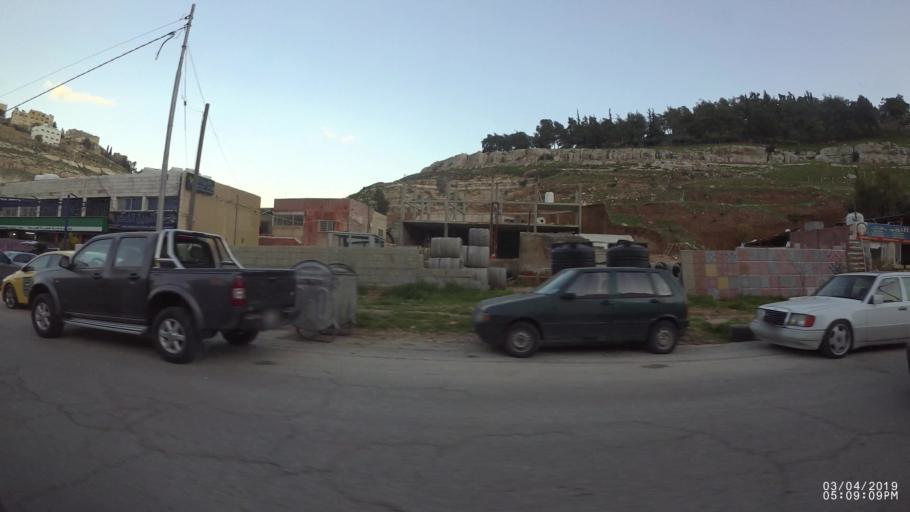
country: JO
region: Amman
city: Al Quwaysimah
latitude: 31.9302
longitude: 35.9209
